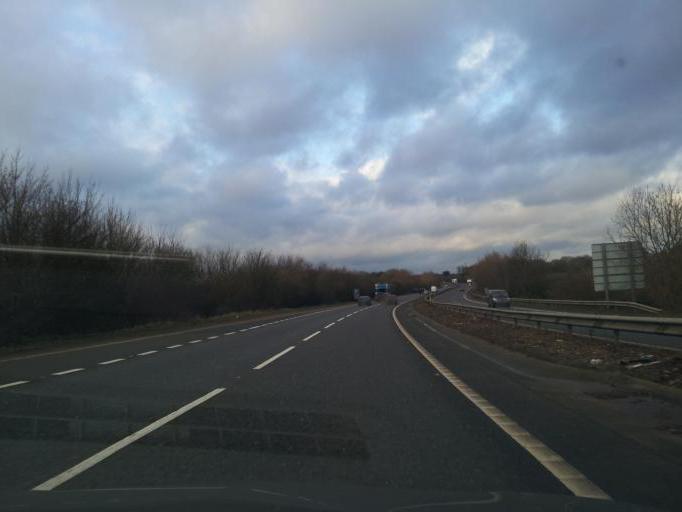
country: GB
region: England
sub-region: Norfolk
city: Bowthorpe
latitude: 52.6296
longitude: 1.1950
